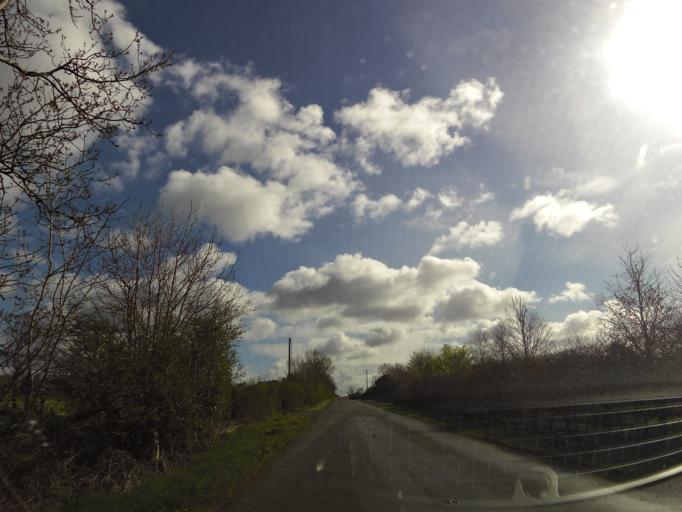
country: IE
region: Connaught
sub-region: Maigh Eo
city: Claremorris
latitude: 53.7773
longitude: -8.9561
